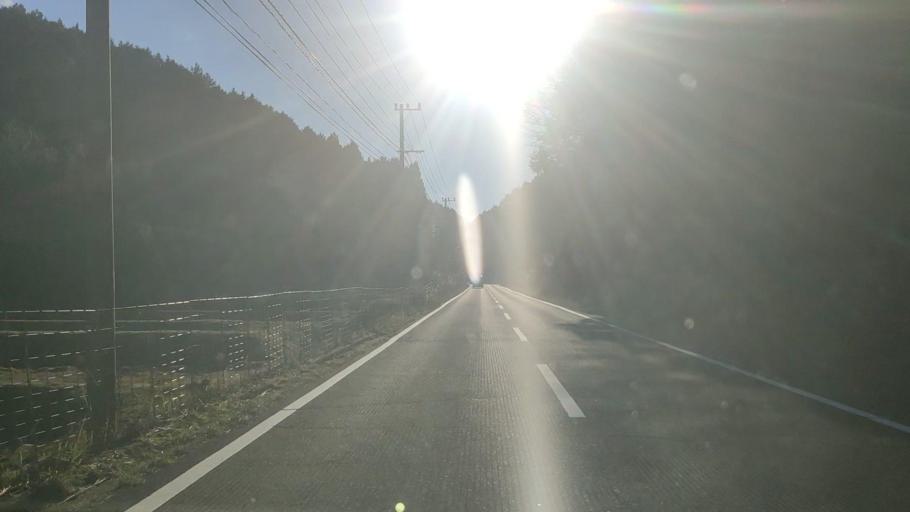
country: JP
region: Saga Prefecture
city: Kanzakimachi-kanzaki
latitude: 33.4150
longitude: 130.2775
